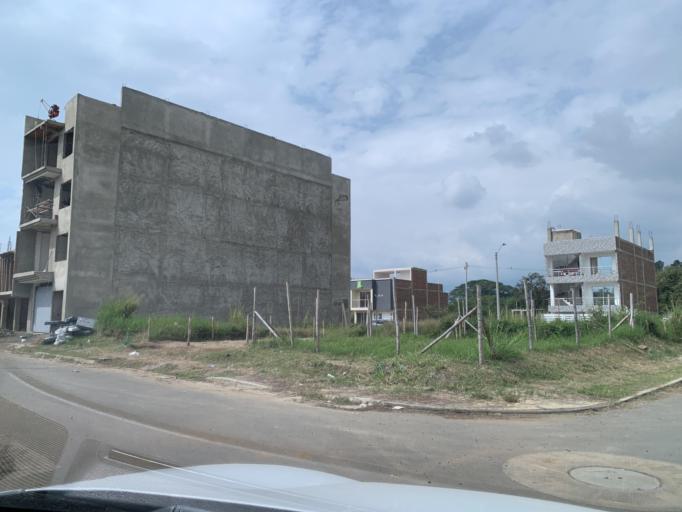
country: CO
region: Valle del Cauca
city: Cali
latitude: 3.3938
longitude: -76.5198
